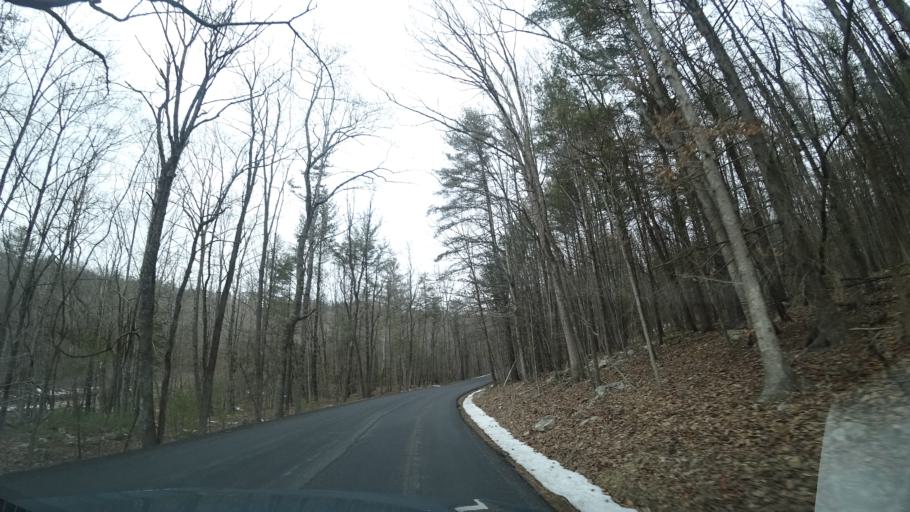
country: US
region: Virginia
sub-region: Shenandoah County
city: Woodstock
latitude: 39.0106
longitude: -78.6673
